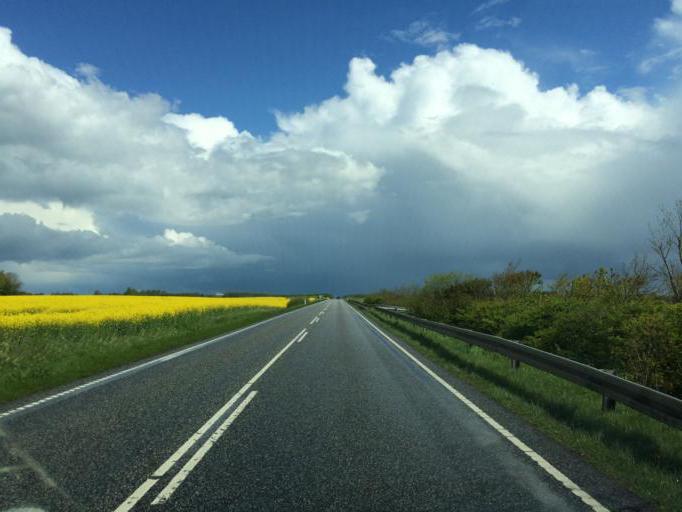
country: DK
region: Central Jutland
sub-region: Holstebro Kommune
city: Vinderup
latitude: 56.4290
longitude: 8.7118
